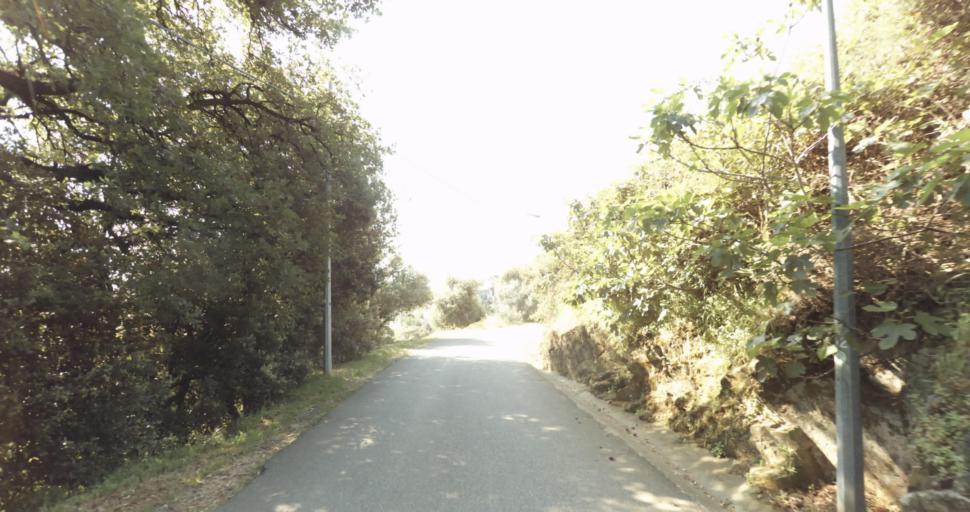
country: FR
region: Corsica
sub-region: Departement de la Haute-Corse
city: Biguglia
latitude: 42.6291
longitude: 9.4187
